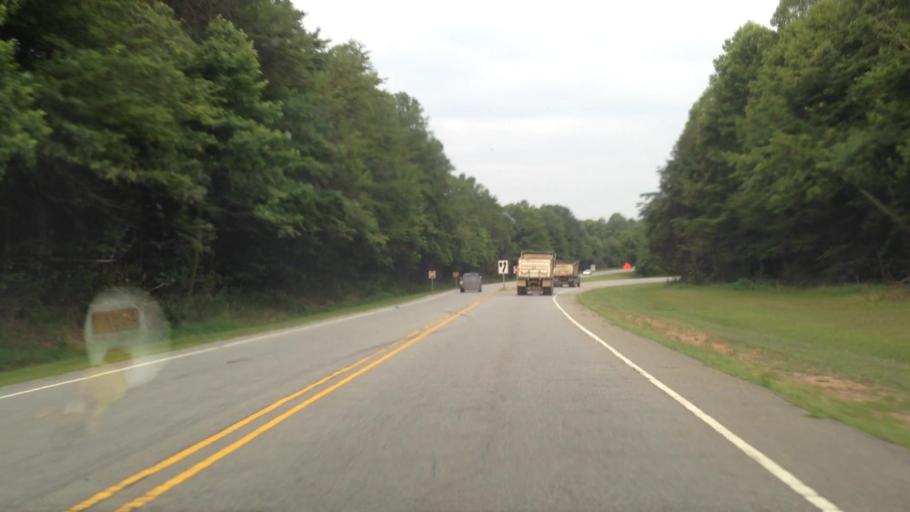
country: US
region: North Carolina
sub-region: Forsyth County
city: Rural Hall
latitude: 36.2032
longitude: -80.2908
